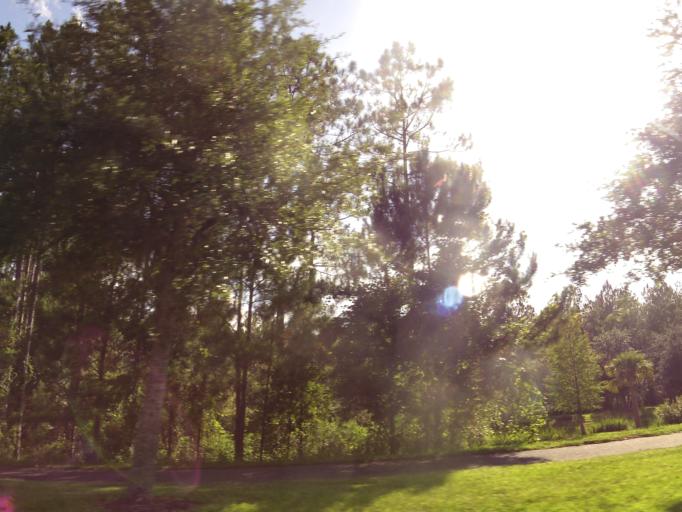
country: US
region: Florida
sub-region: Saint Johns County
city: Fruit Cove
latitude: 30.0397
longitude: -81.6174
